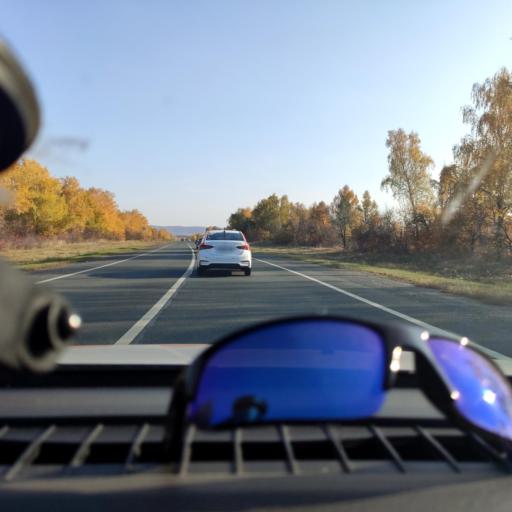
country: RU
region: Samara
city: Volzhskiy
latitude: 53.4764
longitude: 50.1172
